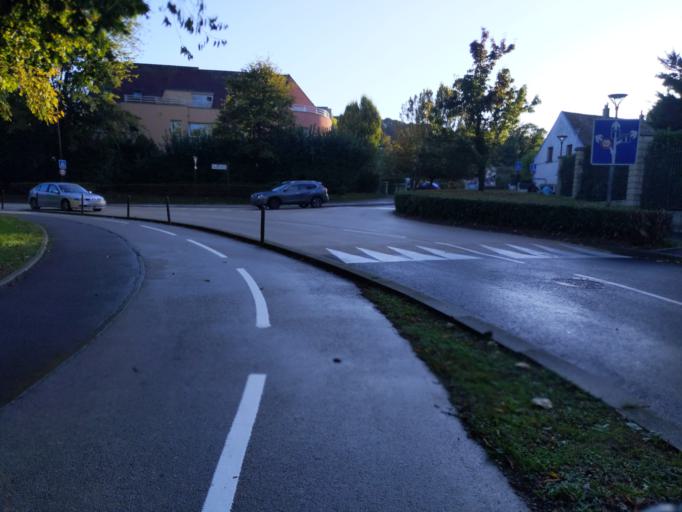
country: FR
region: Ile-de-France
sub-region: Departement des Yvelines
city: Saint-Remy-les-Chevreuse
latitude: 48.7018
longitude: 2.1003
